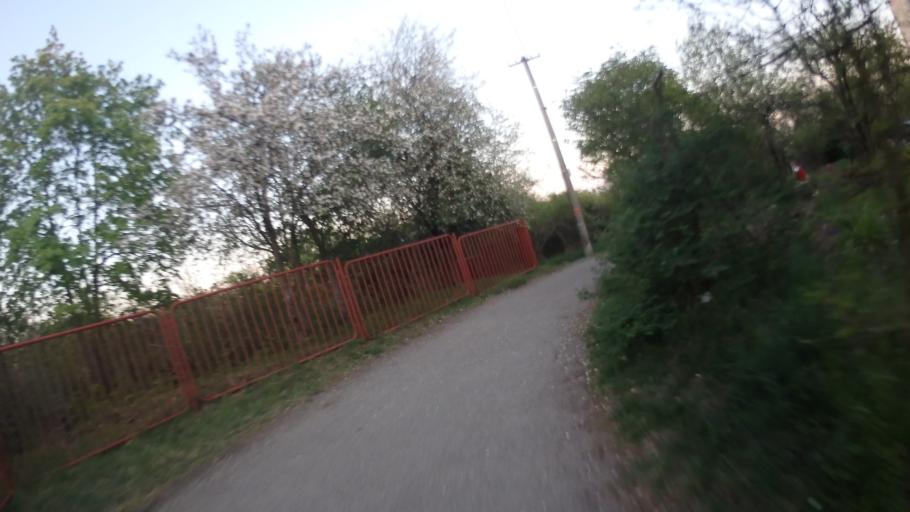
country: CZ
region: South Moravian
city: Ostopovice
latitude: 49.1792
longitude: 16.5552
